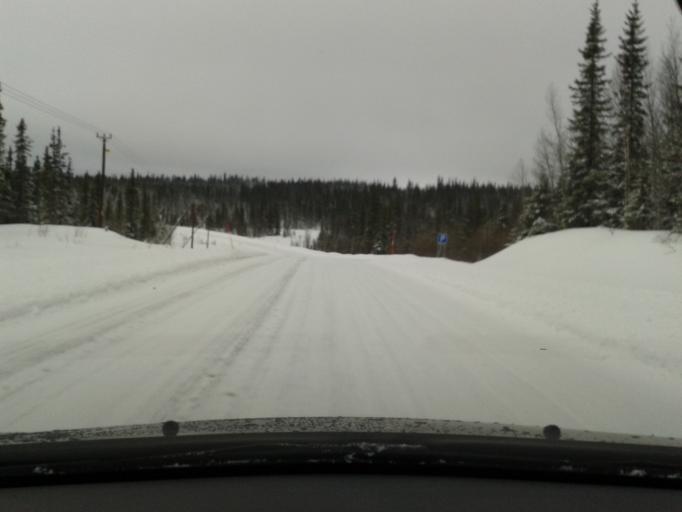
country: SE
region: Vaesterbotten
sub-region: Vilhelmina Kommun
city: Sjoberg
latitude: 65.1943
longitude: 15.9564
